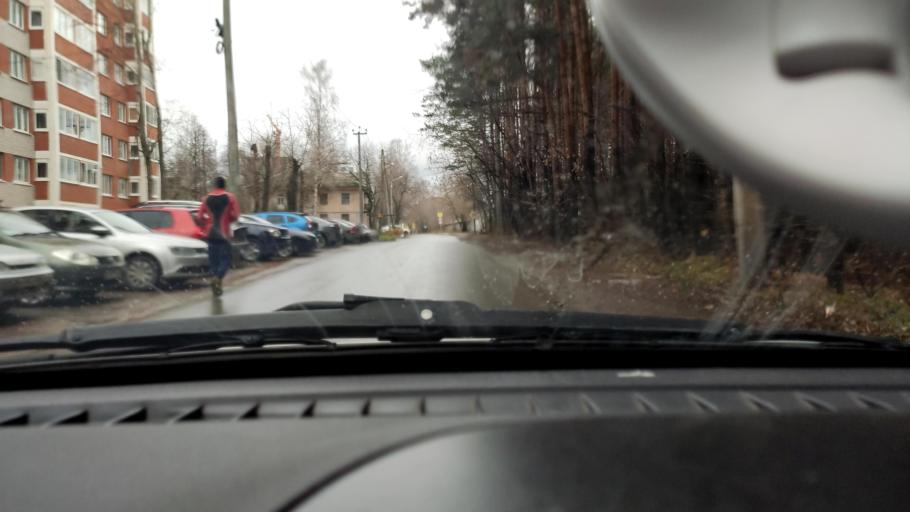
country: RU
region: Perm
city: Perm
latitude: 57.9951
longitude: 56.1810
